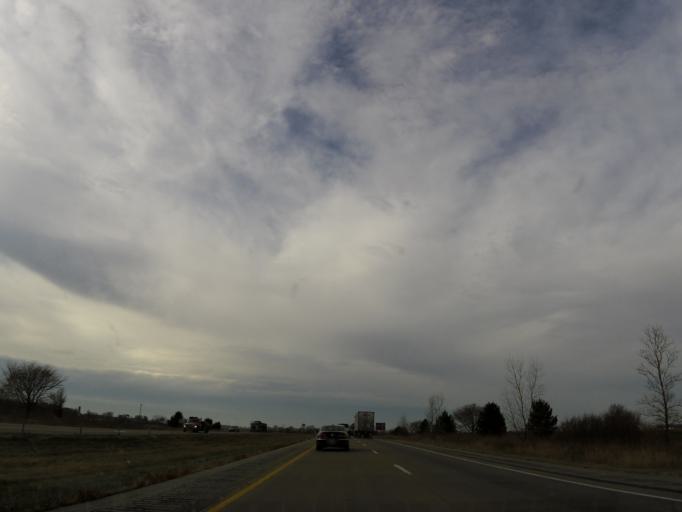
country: US
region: Iowa
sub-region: Scott County
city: Eldridge
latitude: 41.5999
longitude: -90.5986
